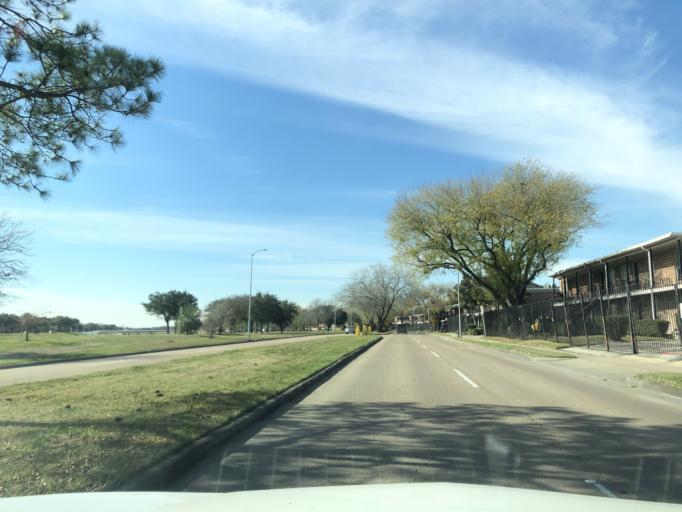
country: US
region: Texas
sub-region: Harris County
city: Bellaire
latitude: 29.6790
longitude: -95.4944
